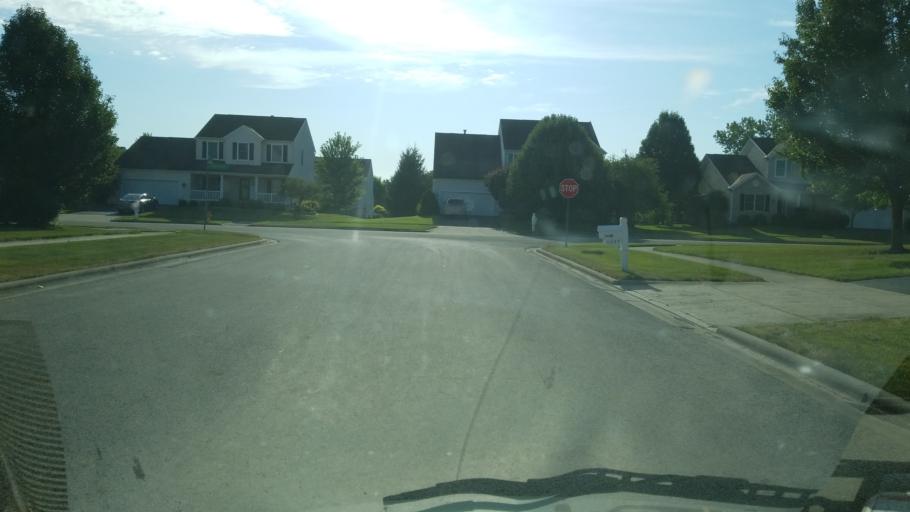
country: US
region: Ohio
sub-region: Delaware County
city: Lewis Center
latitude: 40.1831
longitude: -82.9953
